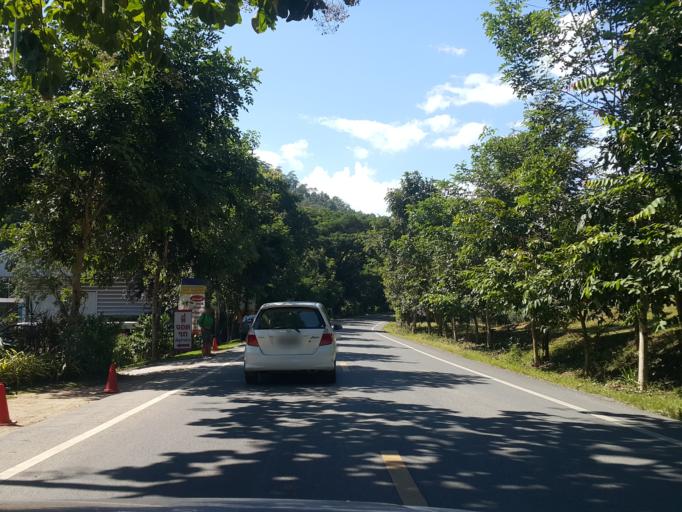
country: TH
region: Chiang Mai
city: Mae Taeng
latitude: 19.1805
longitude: 98.9130
